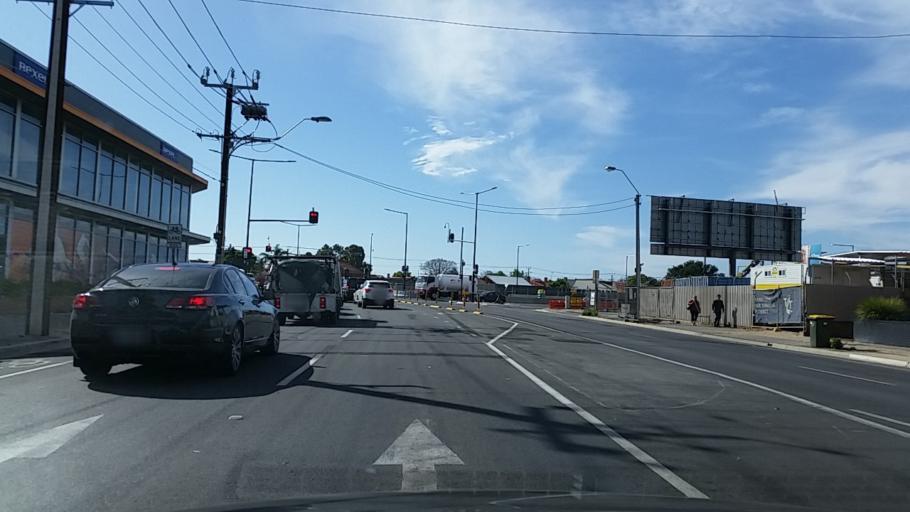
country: AU
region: South Australia
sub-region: City of West Torrens
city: Thebarton
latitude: -34.9049
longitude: 138.5667
